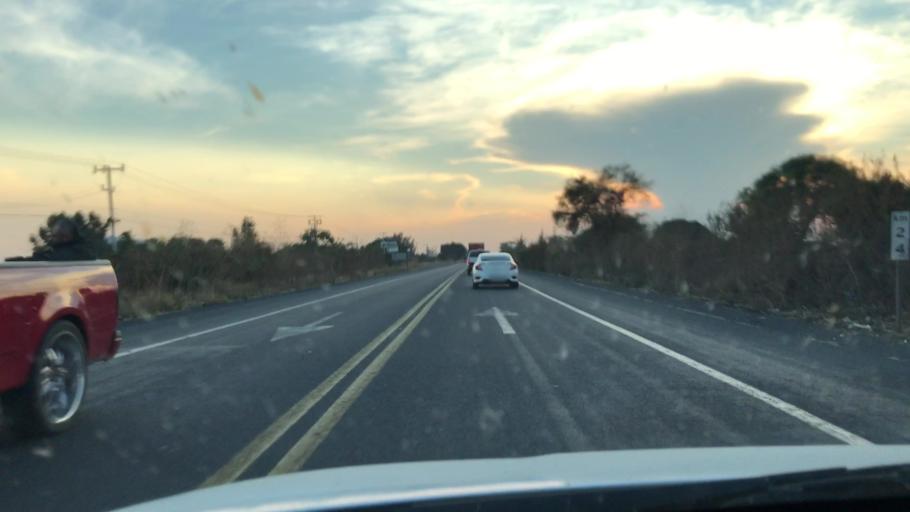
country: MX
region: Michoacan
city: Tanhuato de Guerrero
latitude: 20.3054
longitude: -102.3176
